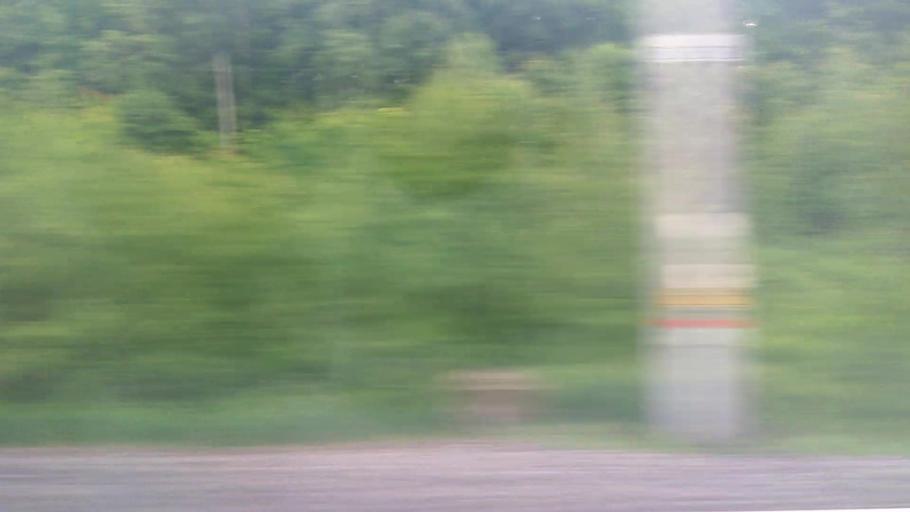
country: RU
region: Moskovskaya
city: Mikhnevo
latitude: 55.0915
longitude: 37.9682
